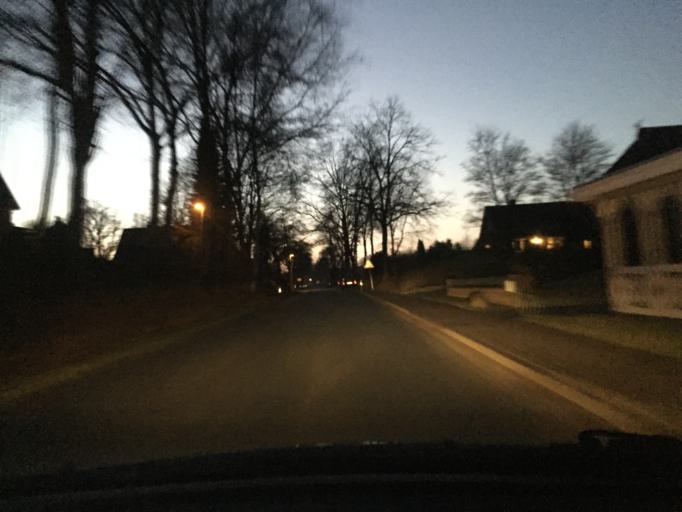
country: DE
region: Lower Saxony
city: Gohrde
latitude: 53.1658
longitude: 10.8613
